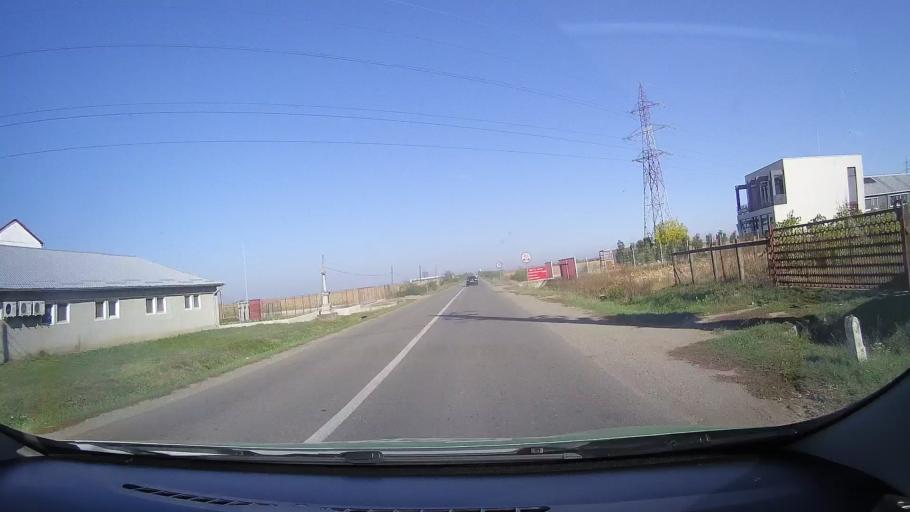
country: RO
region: Satu Mare
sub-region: Oras Tasnad
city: Tasnad
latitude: 47.4961
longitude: 22.5753
